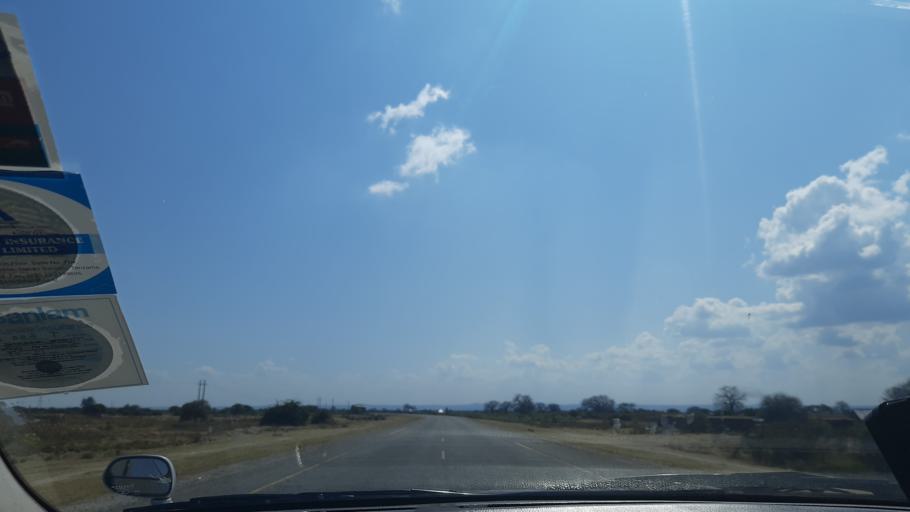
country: TZ
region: Singida
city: Kintinku
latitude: -5.8828
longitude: 35.1403
